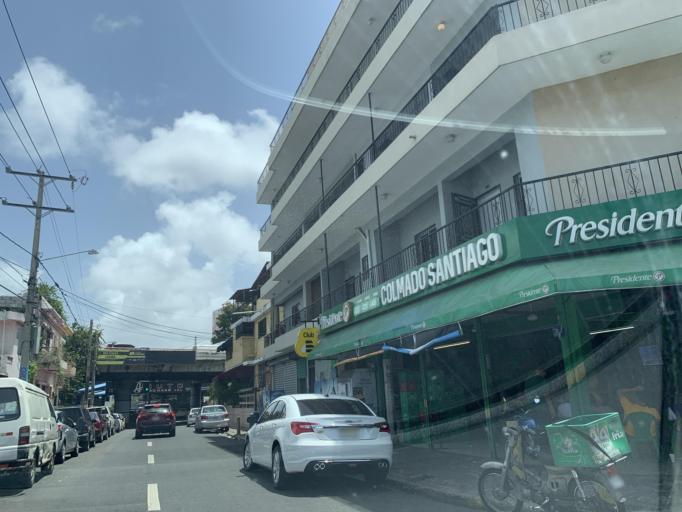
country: DO
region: Nacional
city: San Carlos
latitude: 18.4769
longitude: -69.9031
